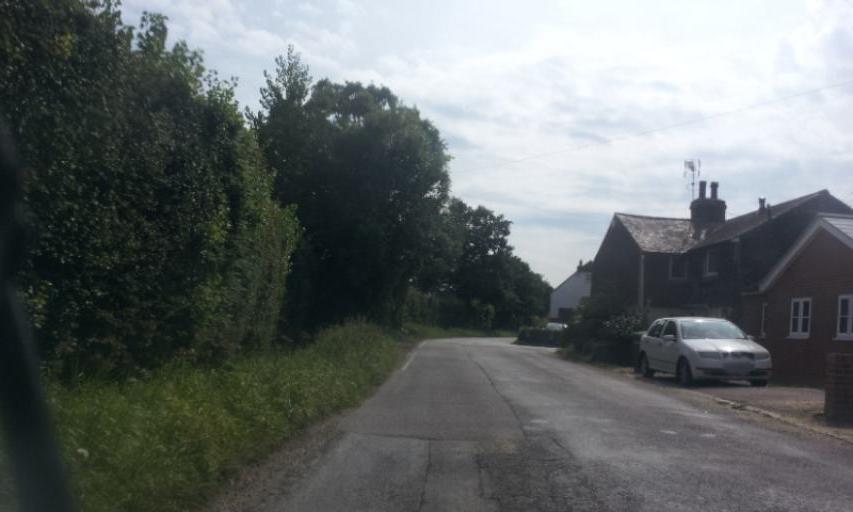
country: GB
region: England
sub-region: Kent
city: Paddock Wood
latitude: 51.1851
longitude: 0.4123
